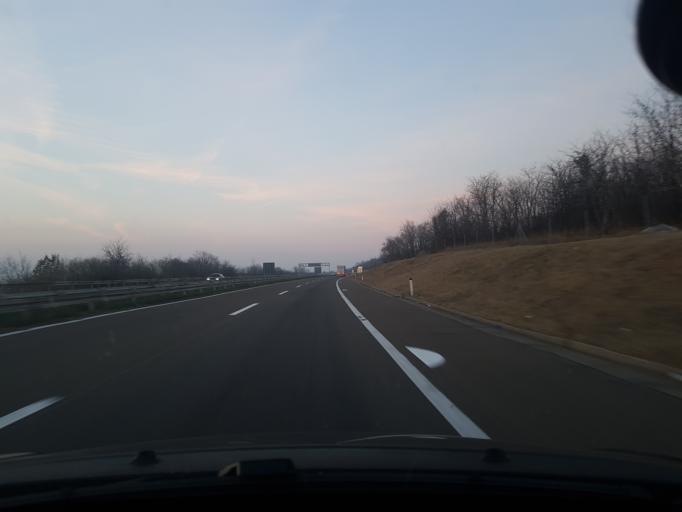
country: RS
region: Central Serbia
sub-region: Rasinski Okrug
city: Cicevac
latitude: 43.7581
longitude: 21.4400
